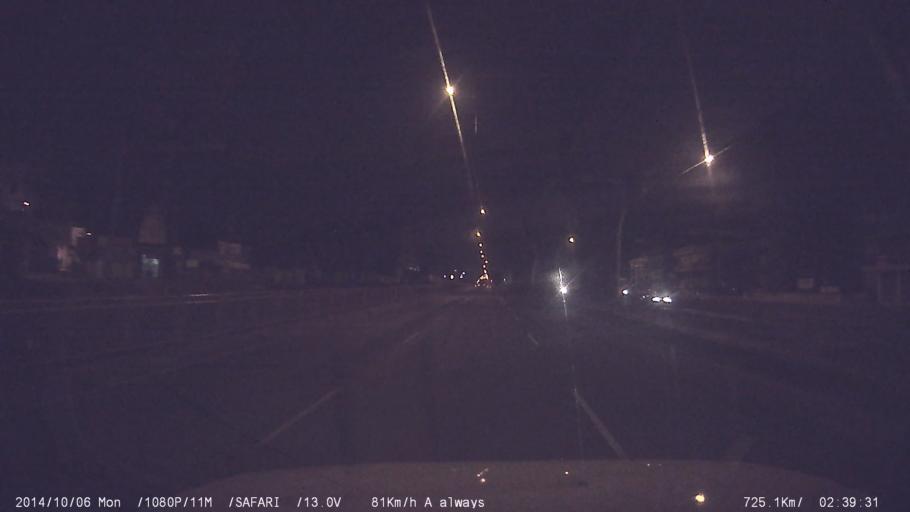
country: IN
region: Karnataka
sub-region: Bangalore Urban
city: Bangalore
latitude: 12.8664
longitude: 77.6560
